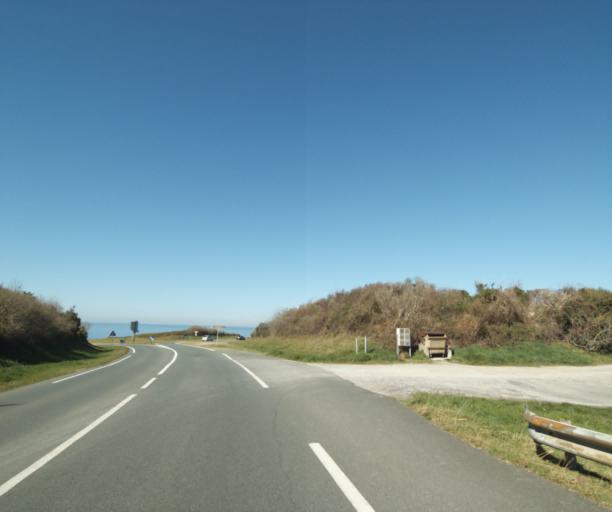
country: FR
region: Aquitaine
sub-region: Departement des Pyrenees-Atlantiques
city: Ciboure
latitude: 43.3899
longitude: -1.7000
